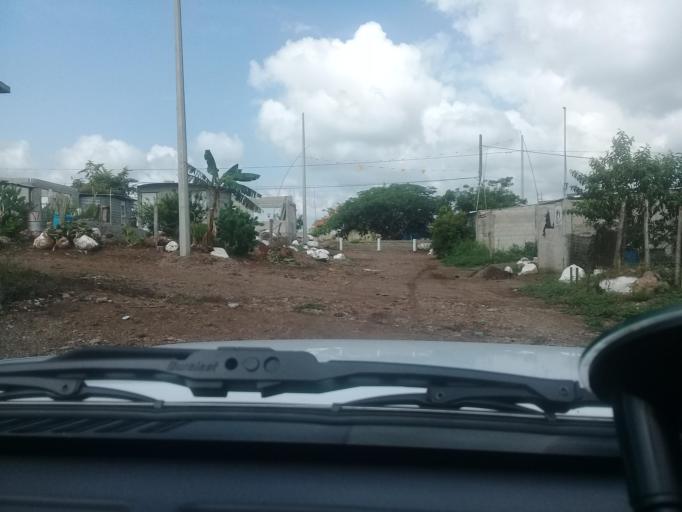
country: MX
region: Veracruz
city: Paso de Ovejas
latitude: 19.2755
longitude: -96.4219
